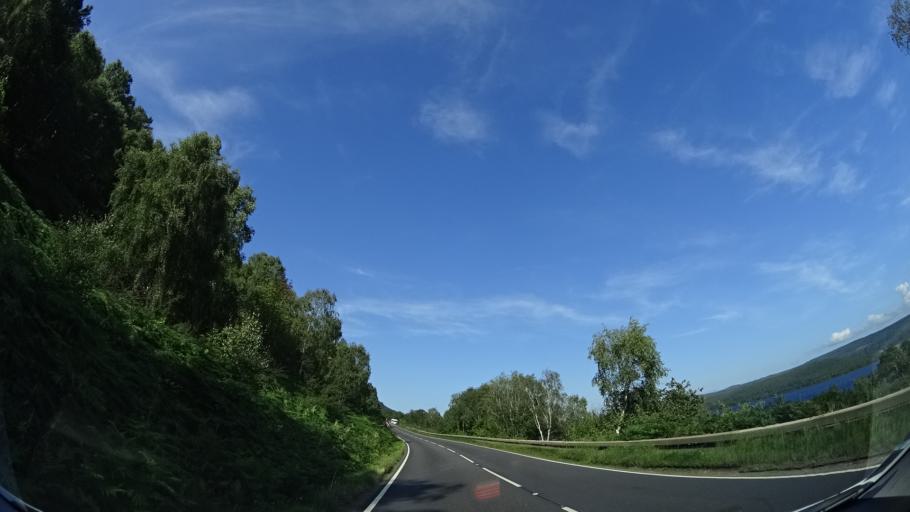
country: GB
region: Scotland
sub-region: Highland
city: Beauly
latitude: 57.3867
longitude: -4.3698
